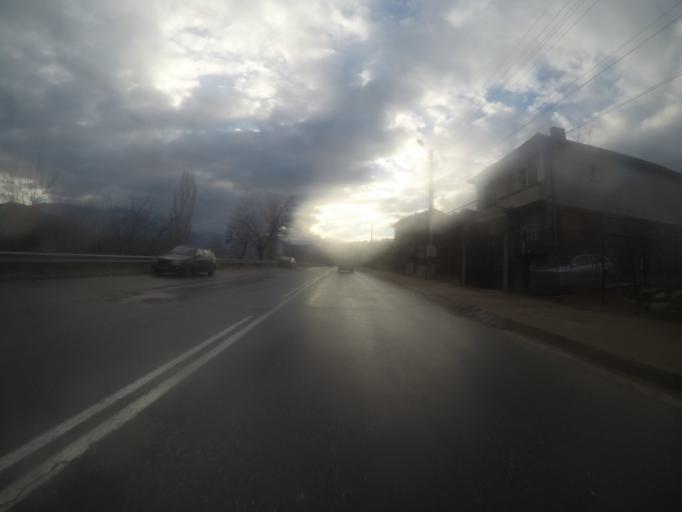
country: BG
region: Blagoevgrad
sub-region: Obshtina Simitli
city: Simitli
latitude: 41.8843
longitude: 23.1202
